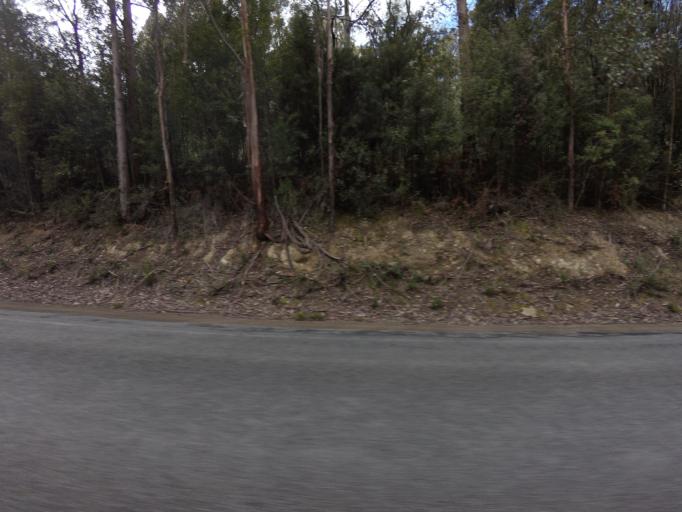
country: AU
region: Tasmania
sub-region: Huon Valley
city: Cygnet
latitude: -43.2758
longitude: 147.0089
